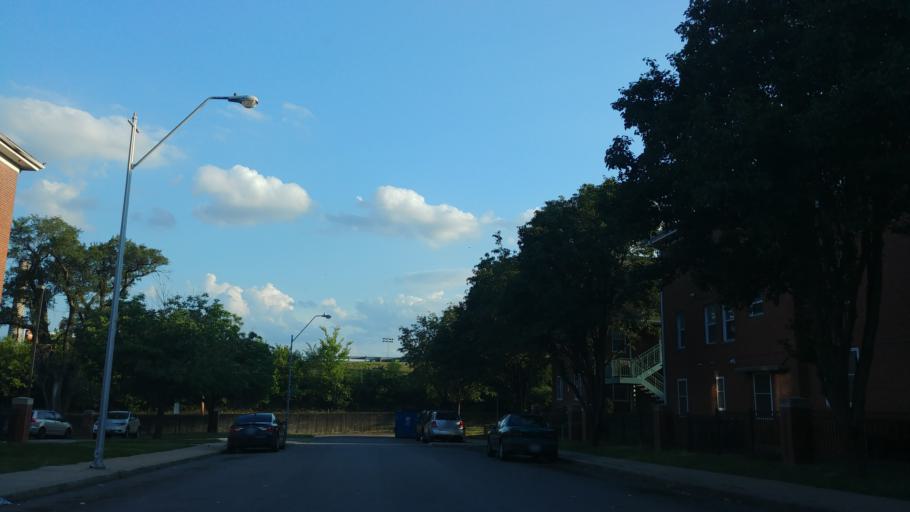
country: US
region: Missouri
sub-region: Jackson County
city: Kansas City
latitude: 39.0970
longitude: -94.5631
